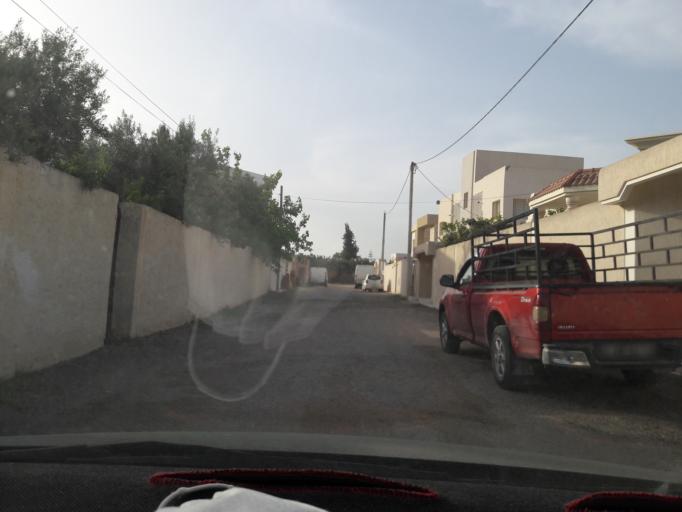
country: TN
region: Safaqis
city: Al Qarmadah
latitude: 34.8029
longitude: 10.7505
